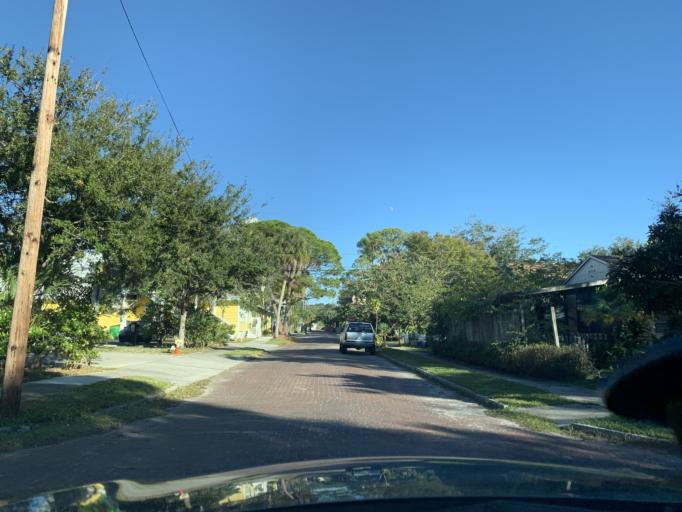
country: US
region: Florida
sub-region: Pinellas County
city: Gulfport
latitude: 27.7401
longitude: -82.7087
